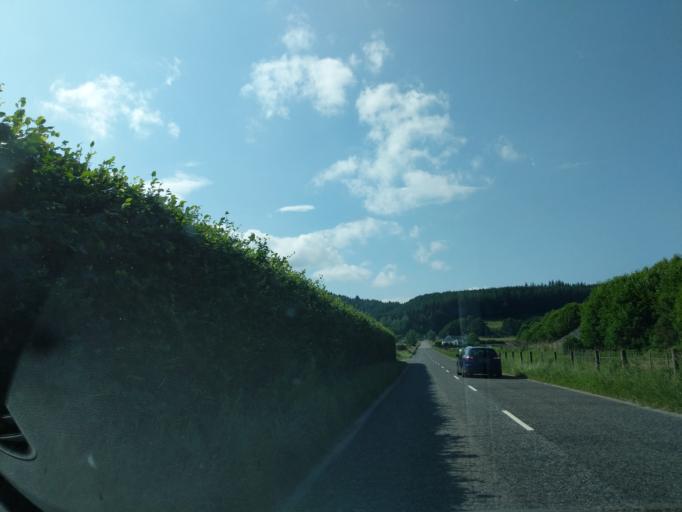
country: GB
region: Scotland
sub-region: Moray
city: Rothes
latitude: 57.5517
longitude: -3.1449
